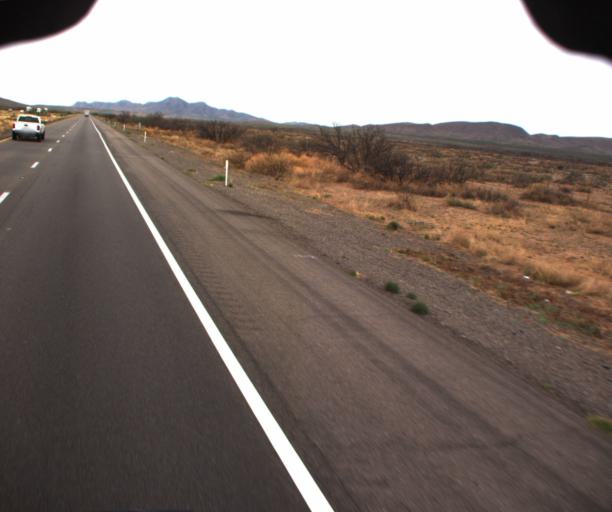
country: US
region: Arizona
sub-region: Cochise County
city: Willcox
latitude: 32.1720
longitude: -109.9573
